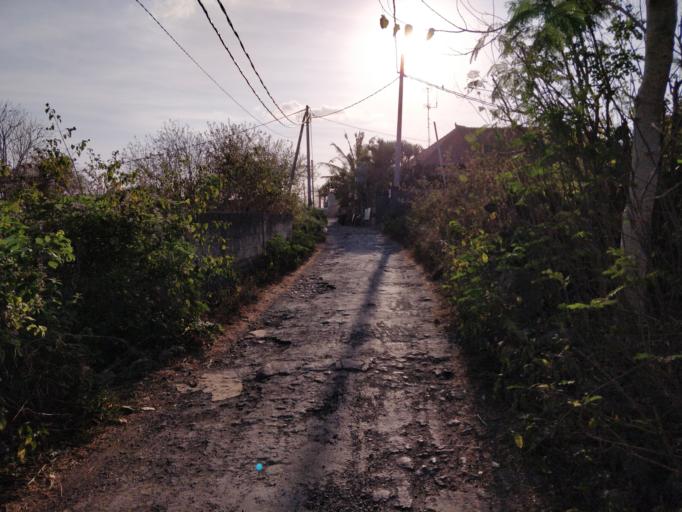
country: ID
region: Bali
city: Lembongan Kawan
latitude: -8.6841
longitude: 115.4303
